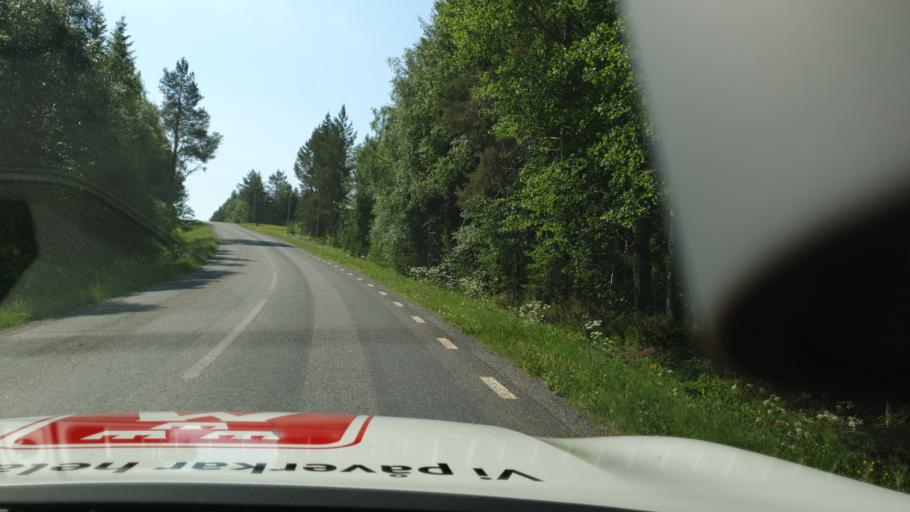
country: SE
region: Vaesterbotten
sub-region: Skelleftea Kommun
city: Langsele
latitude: 65.0013
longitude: 20.0910
